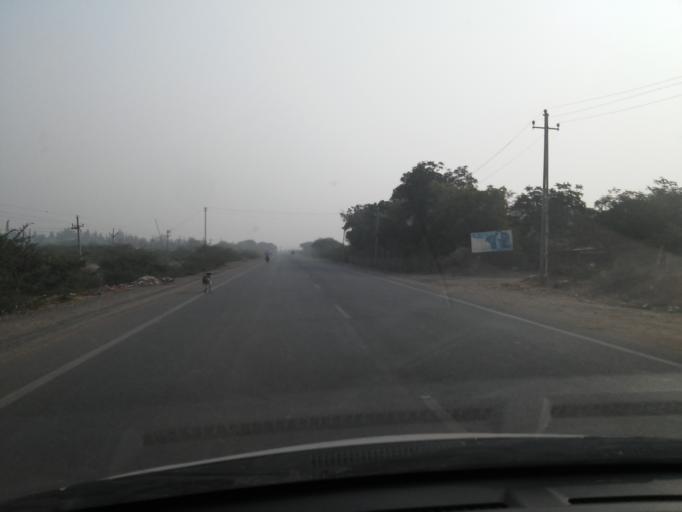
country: IN
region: Gujarat
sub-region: Kachchh
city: Bhuj
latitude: 23.2310
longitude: 69.7668
